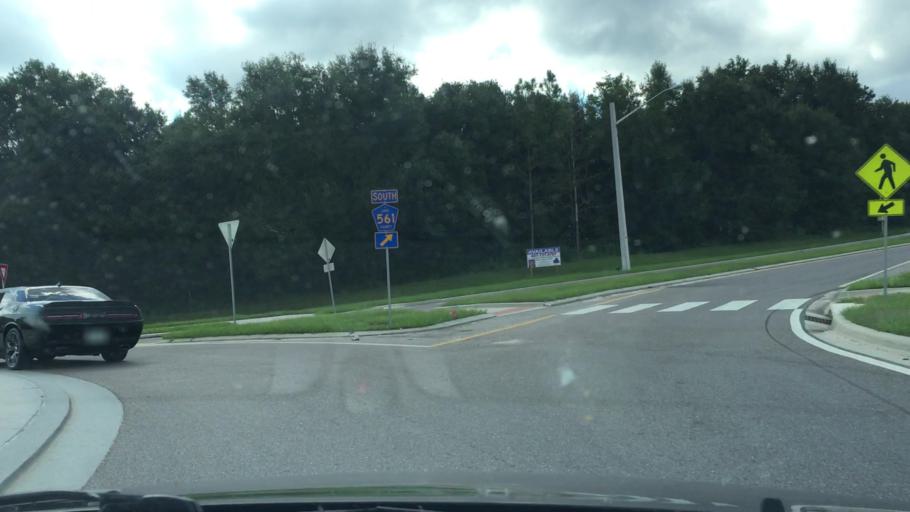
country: US
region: Florida
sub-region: Lake County
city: Astatula
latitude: 28.6667
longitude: -81.7376
